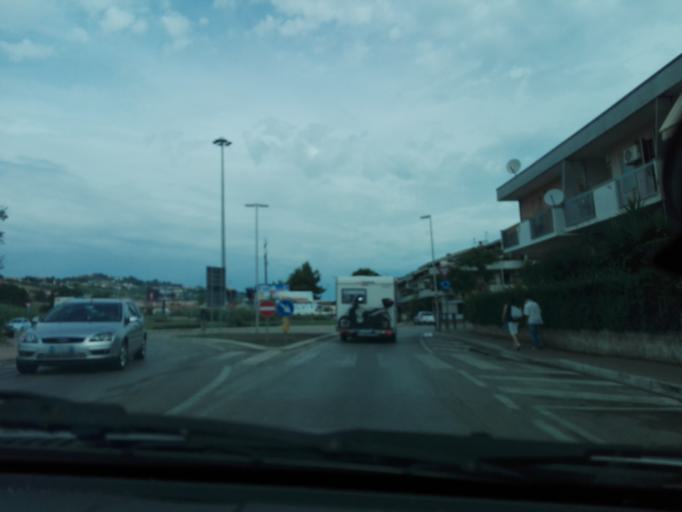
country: IT
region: Abruzzo
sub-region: Provincia di Teramo
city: Silvi
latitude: 42.5412
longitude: 14.1242
